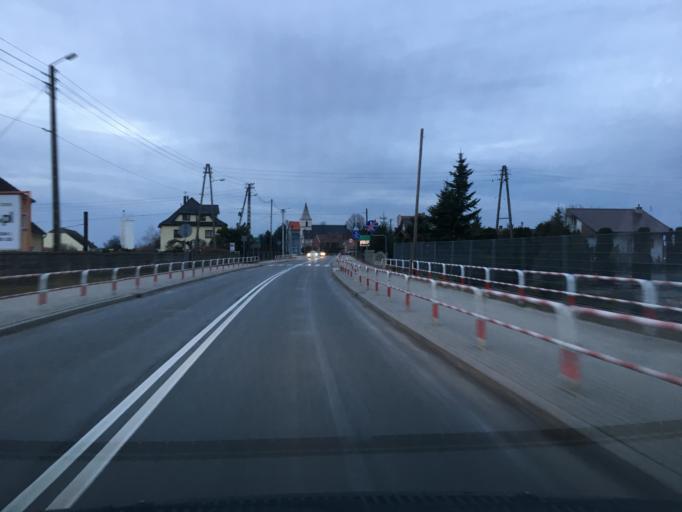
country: PL
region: Opole Voivodeship
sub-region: Powiat opolski
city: Proszkow
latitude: 50.5890
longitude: 17.9316
